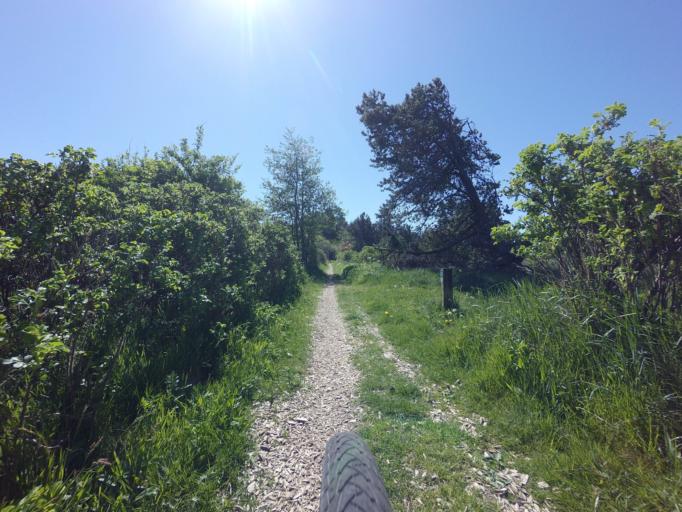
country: DK
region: North Denmark
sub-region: Jammerbugt Kommune
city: Pandrup
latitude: 57.2596
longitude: 9.6205
